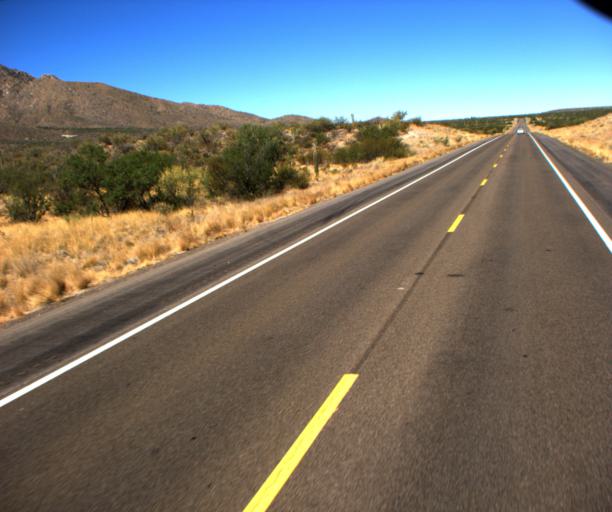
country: US
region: Arizona
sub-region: Pima County
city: Three Points
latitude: 32.0371
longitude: -111.5215
